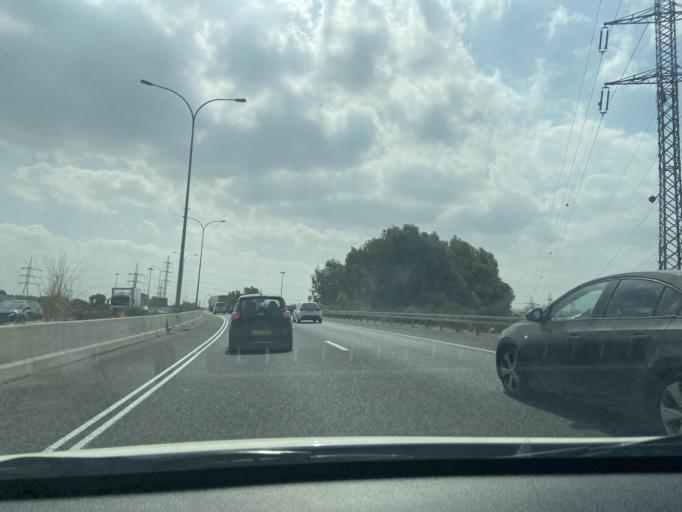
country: IL
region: Haifa
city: Qiryat Yam
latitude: 32.8766
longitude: 35.0967
